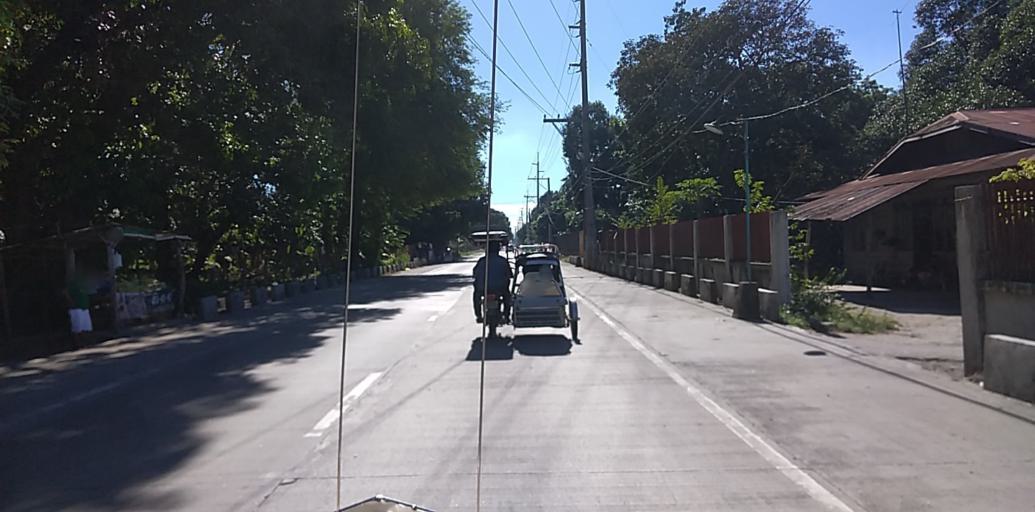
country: PH
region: Central Luzon
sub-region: Province of Pampanga
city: Santo Domingo
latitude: 15.0662
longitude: 120.7675
